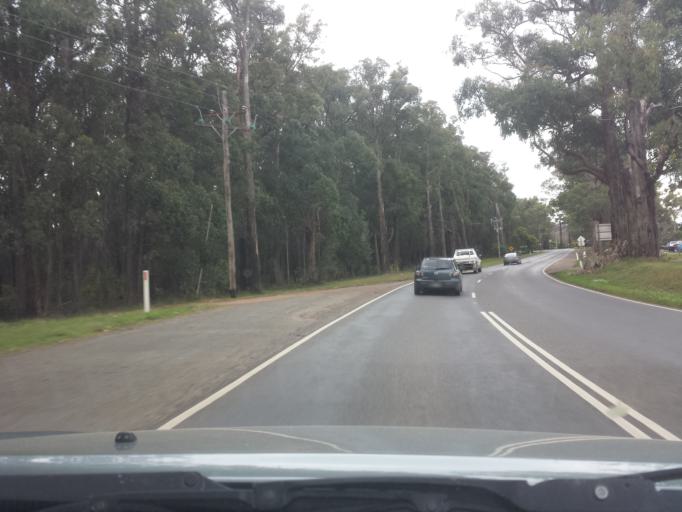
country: AU
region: Victoria
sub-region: Yarra Ranges
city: Kalorama
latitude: -37.8224
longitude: 145.4138
